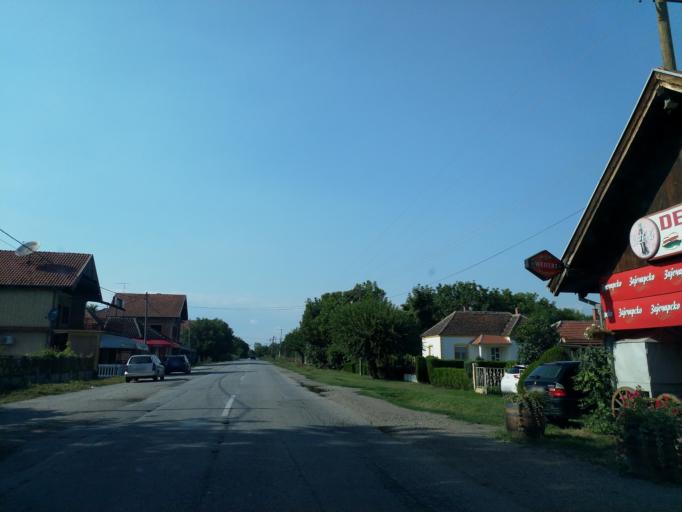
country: RS
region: Central Serbia
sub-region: Rasinski Okrug
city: Cicevac
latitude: 43.7654
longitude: 21.4291
